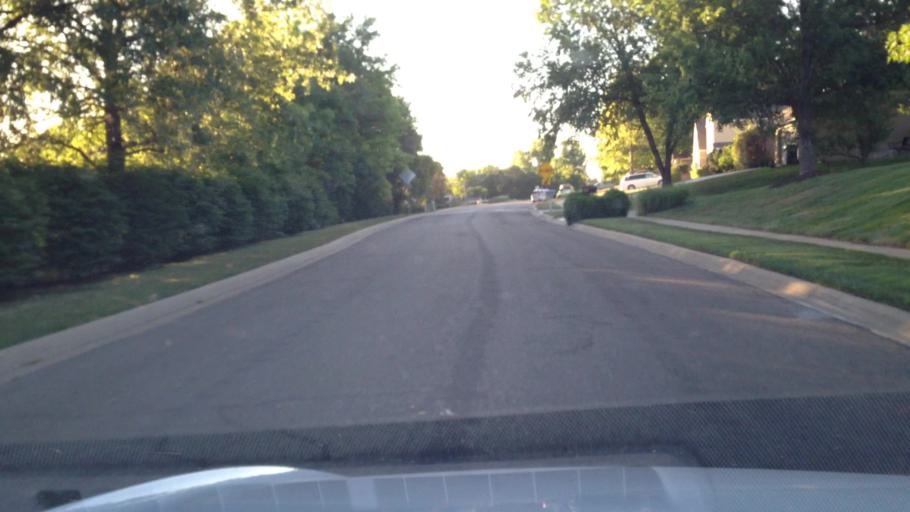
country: US
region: Kansas
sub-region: Douglas County
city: Lawrence
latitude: 38.9443
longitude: -95.2888
